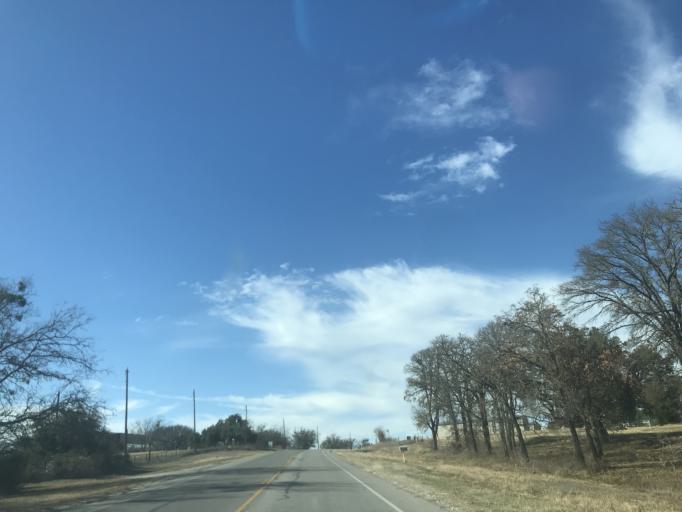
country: US
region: Texas
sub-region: Erath County
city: Stephenville
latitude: 32.2068
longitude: -98.1911
